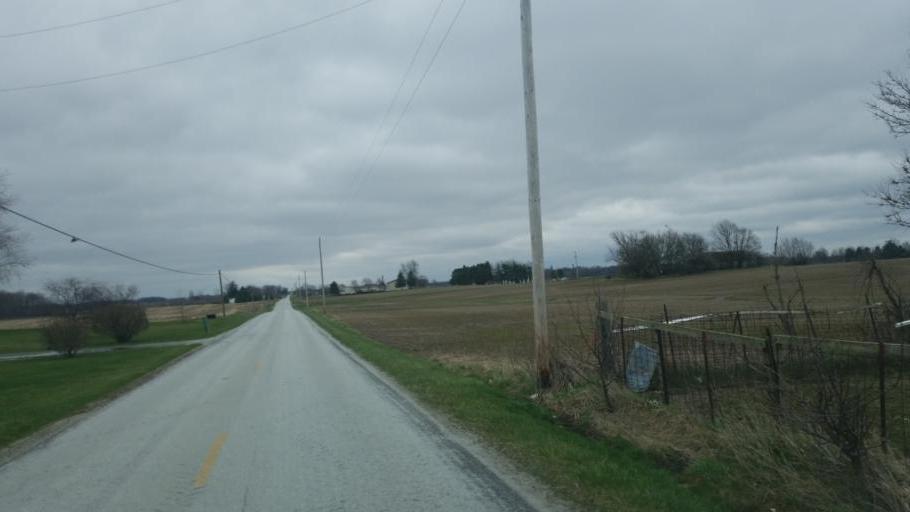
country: US
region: Ohio
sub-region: Hardin County
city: Kenton
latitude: 40.6589
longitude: -83.5676
